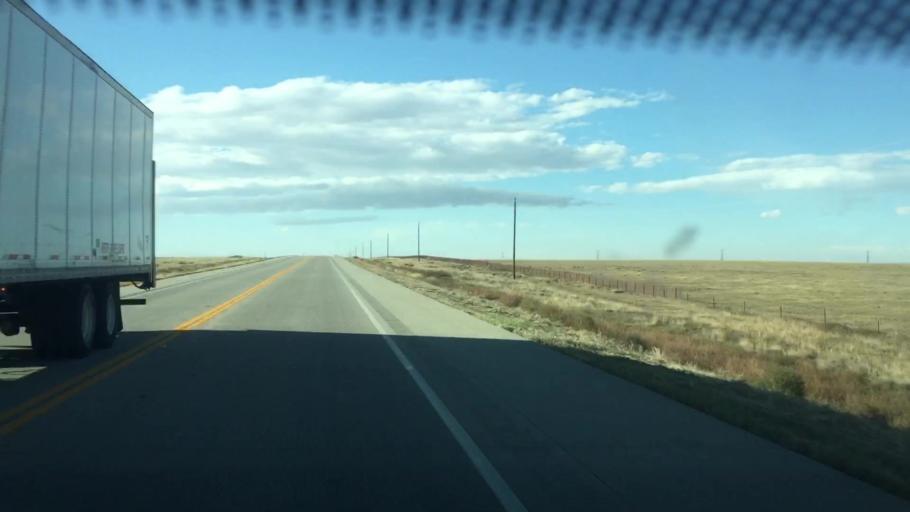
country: US
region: Colorado
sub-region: Lincoln County
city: Hugo
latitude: 39.0772
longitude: -103.3831
